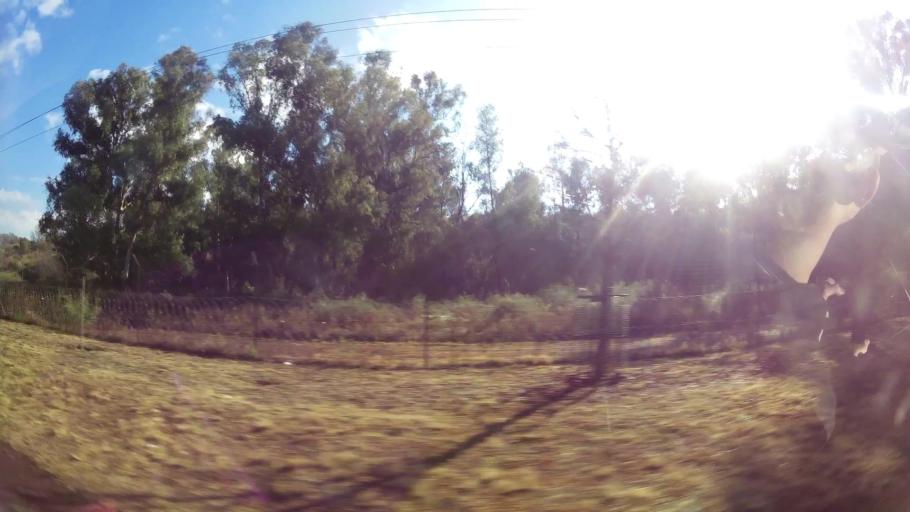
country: ZA
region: Gauteng
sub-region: Sedibeng District Municipality
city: Meyerton
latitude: -26.5265
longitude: 28.0543
